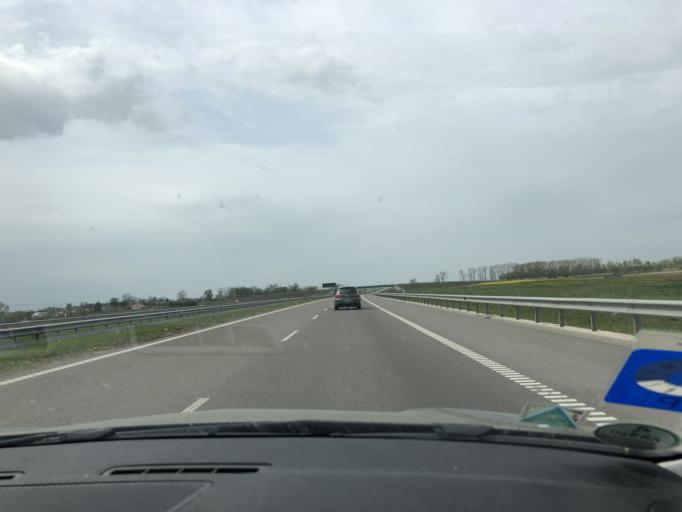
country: PL
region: Subcarpathian Voivodeship
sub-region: Powiat przemyski
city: Stubno
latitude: 49.9446
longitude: 23.0051
